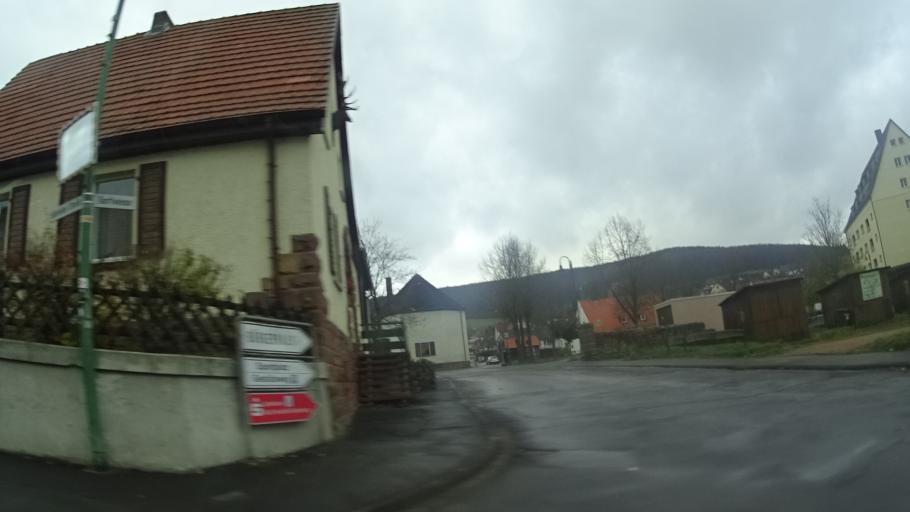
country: DE
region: Thuringia
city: Buttlar
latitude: 50.7831
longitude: 9.9139
